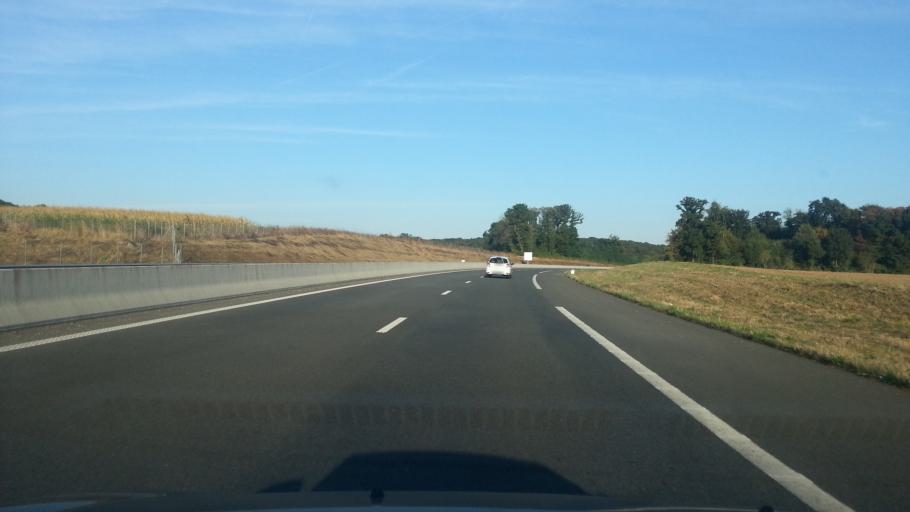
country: FR
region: Picardie
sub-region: Departement de l'Oise
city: Breuil-le-Sec
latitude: 49.3858
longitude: 2.4630
